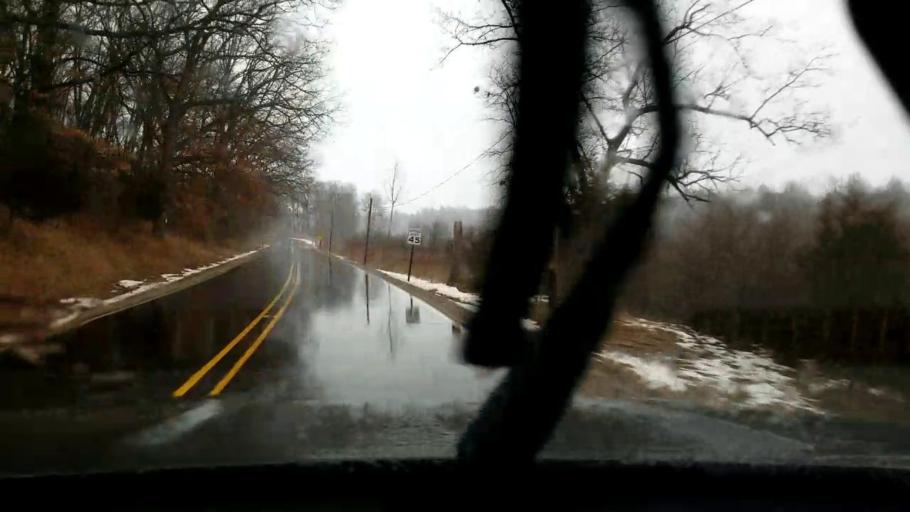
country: US
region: Michigan
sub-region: Jackson County
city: Grass Lake
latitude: 42.3251
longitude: -84.2085
